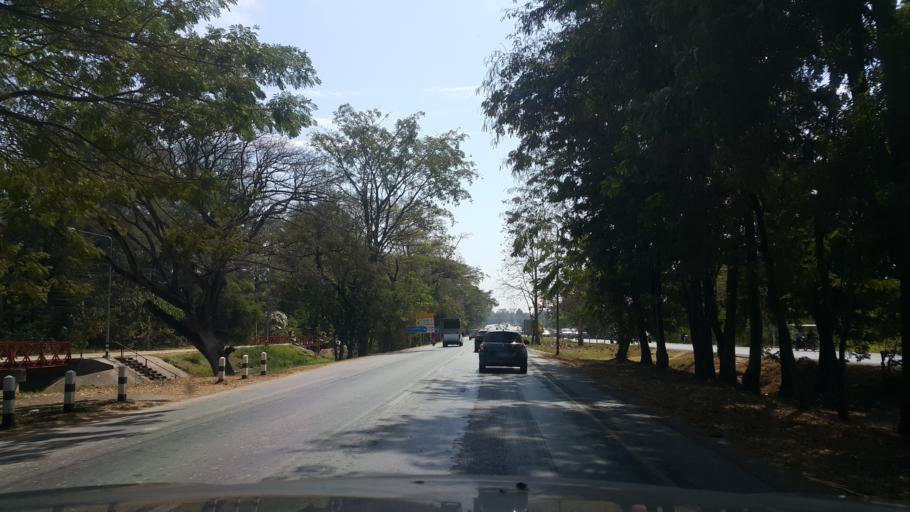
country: TH
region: Nakhon Ratchasima
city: Nakhon Ratchasima
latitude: 14.9188
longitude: 102.0641
